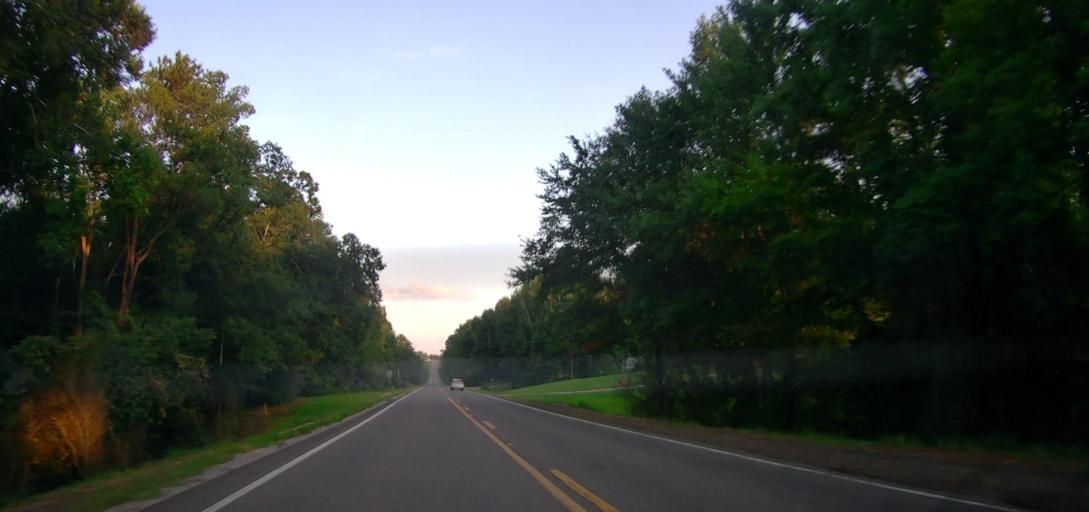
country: US
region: Alabama
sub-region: Marion County
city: Hamilton
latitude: 34.0956
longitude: -87.9869
